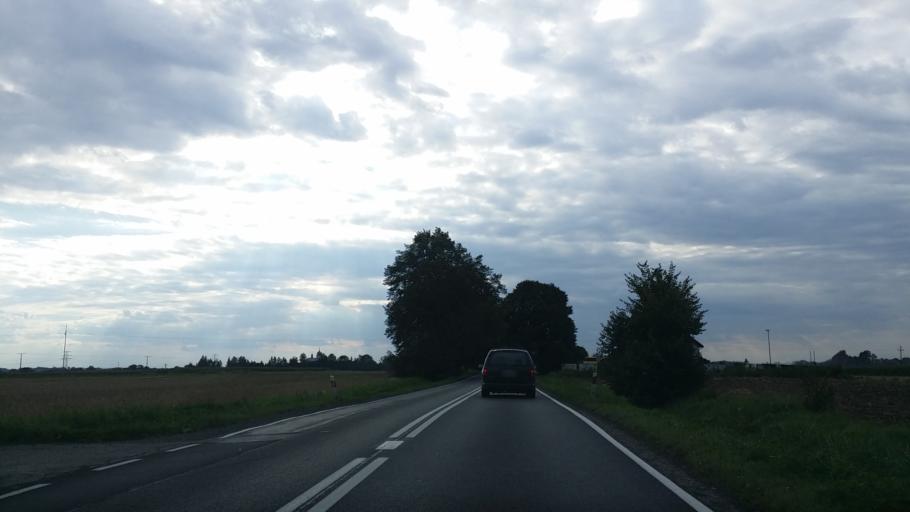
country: PL
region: Lesser Poland Voivodeship
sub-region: Powiat oswiecimski
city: Przeciszow
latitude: 50.0043
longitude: 19.3875
